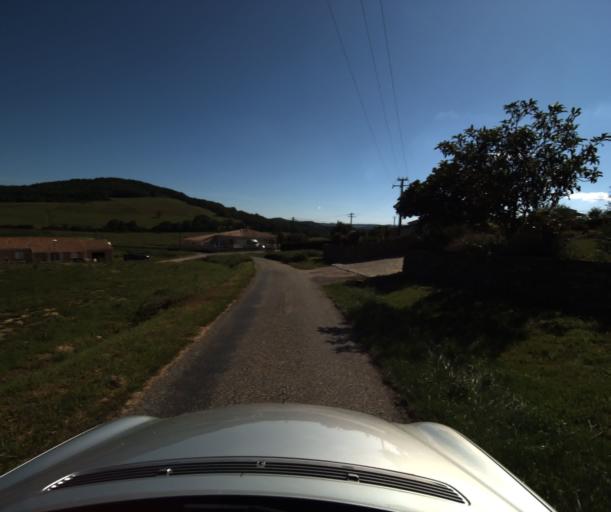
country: FR
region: Midi-Pyrenees
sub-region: Departement de l'Ariege
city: Lavelanet
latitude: 42.9898
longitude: 1.8864
